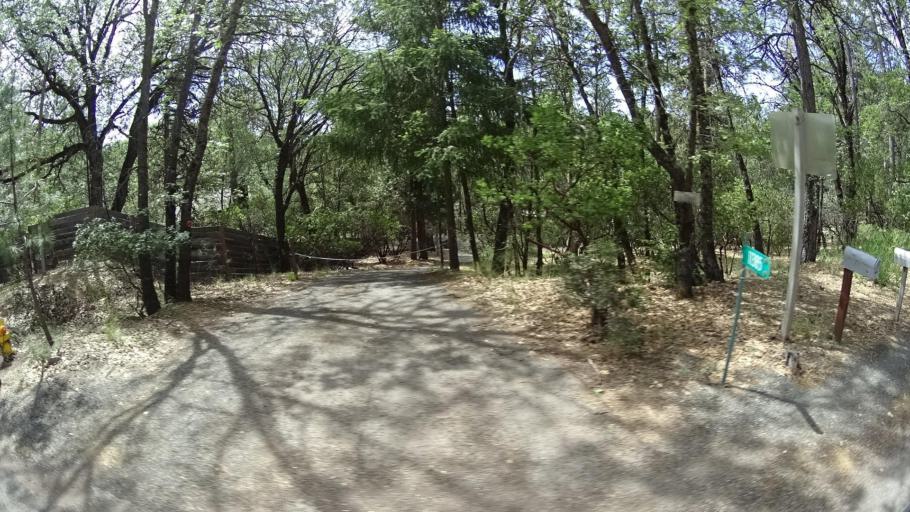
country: US
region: California
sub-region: Lake County
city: Cobb
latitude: 38.8647
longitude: -122.6988
